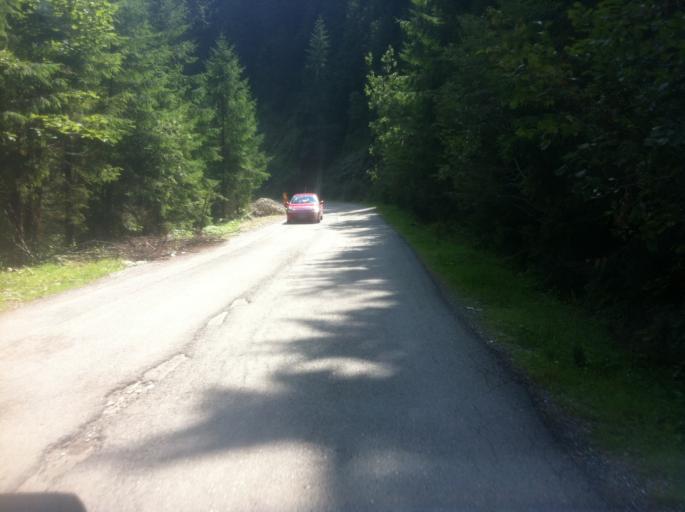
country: RO
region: Hunedoara
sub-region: Oras Petrila
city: Petrila
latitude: 45.4084
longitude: 23.5297
